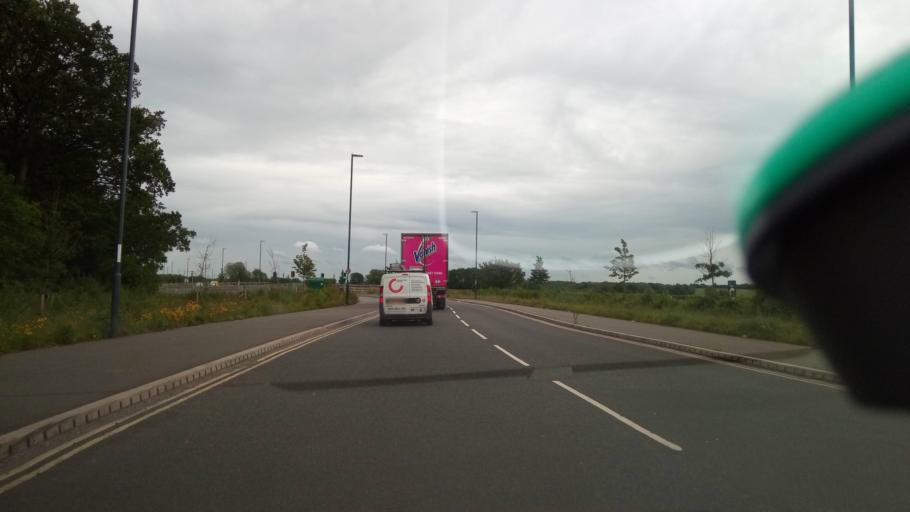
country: GB
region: England
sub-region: Derby
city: Derby
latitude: 52.8763
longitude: -1.4655
